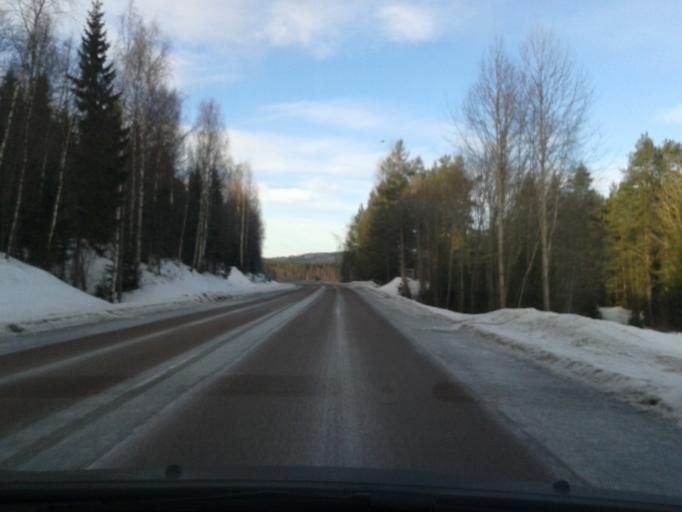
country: SE
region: Vaesternorrland
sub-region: OErnskoeldsviks Kommun
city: Bjasta
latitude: 63.3450
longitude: 18.5019
